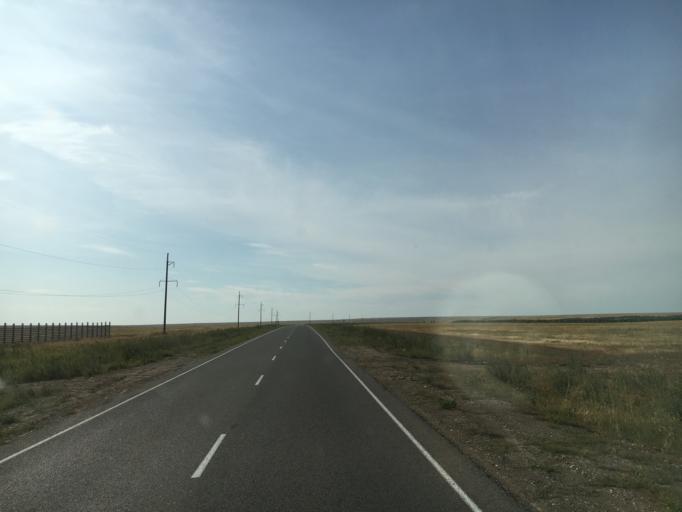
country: KZ
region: Batys Qazaqstan
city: Kamenka
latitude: 51.1447
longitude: 50.0942
